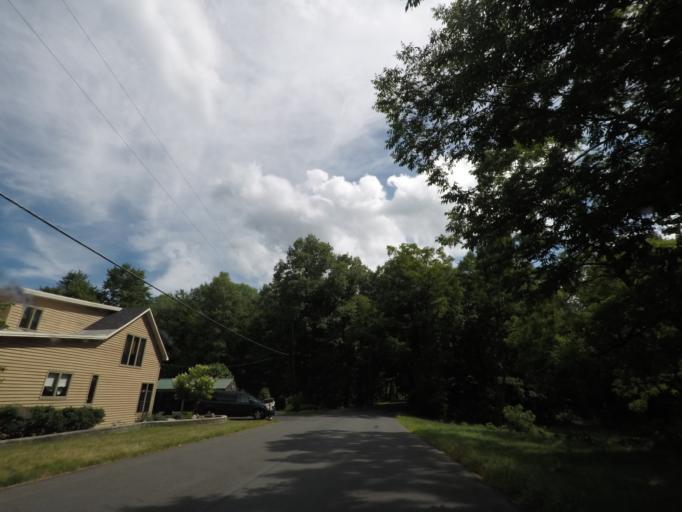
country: US
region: New York
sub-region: Rensselaer County
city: Averill Park
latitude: 42.6504
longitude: -73.5493
